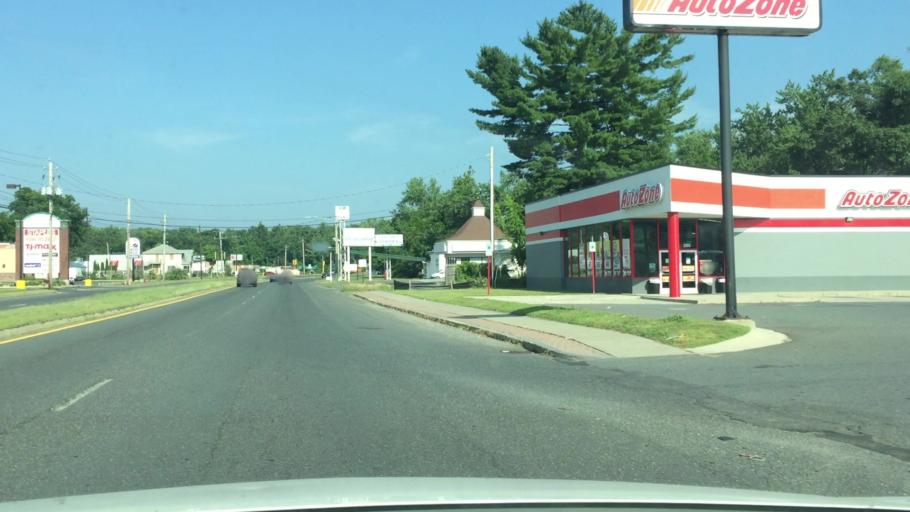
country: US
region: Massachusetts
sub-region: Hampden County
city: Westfield
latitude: 42.1147
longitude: -72.7291
